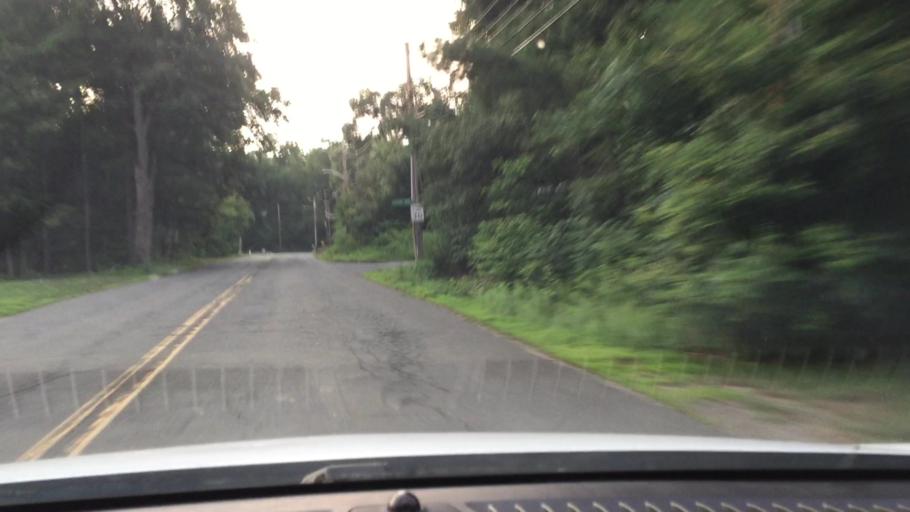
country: US
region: Massachusetts
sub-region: Hampden County
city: Westfield
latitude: 42.1380
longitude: -72.8102
